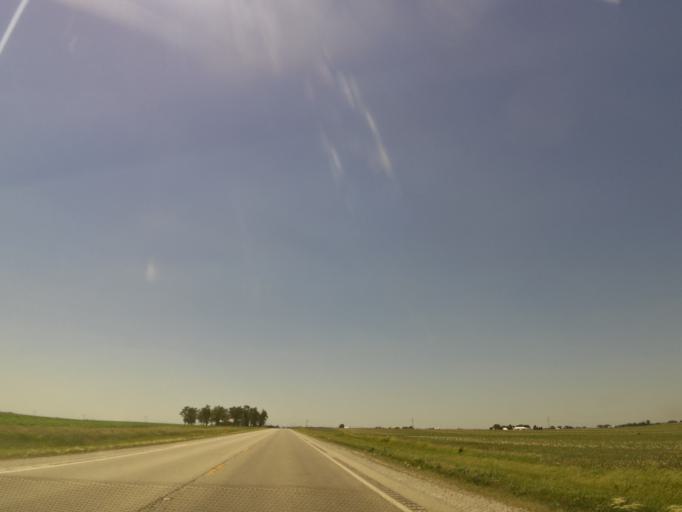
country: US
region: Illinois
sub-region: McLean County
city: Chenoa
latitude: 40.7421
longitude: -88.6612
